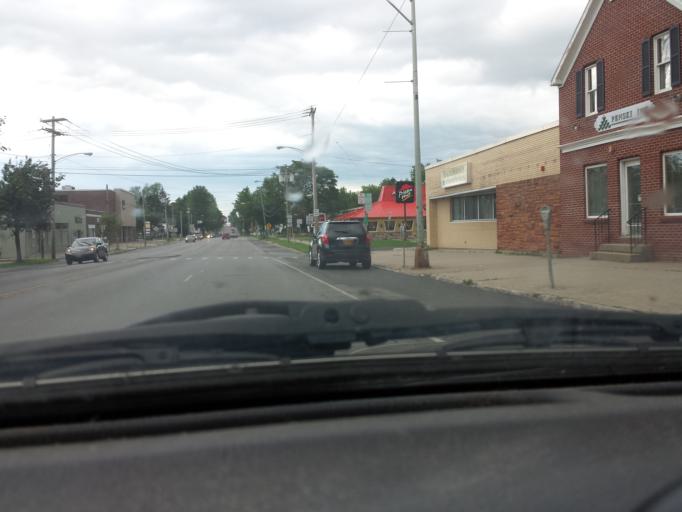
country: US
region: New York
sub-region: St. Lawrence County
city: Potsdam
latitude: 44.6706
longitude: -74.9868
